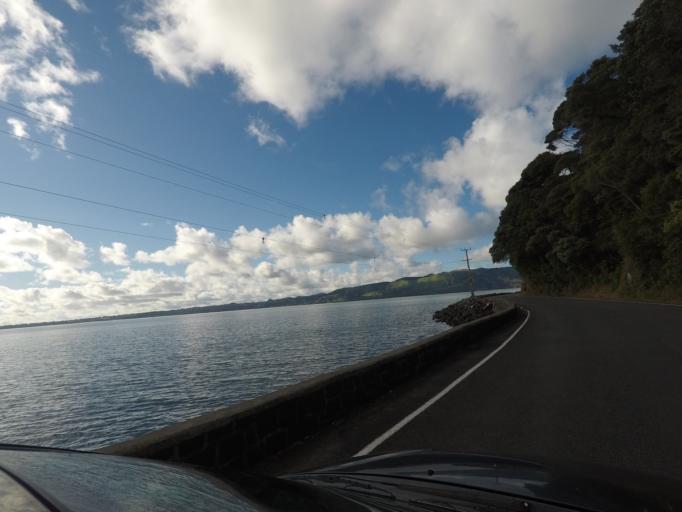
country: NZ
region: Auckland
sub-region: Auckland
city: Titirangi
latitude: -37.0099
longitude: 174.5626
